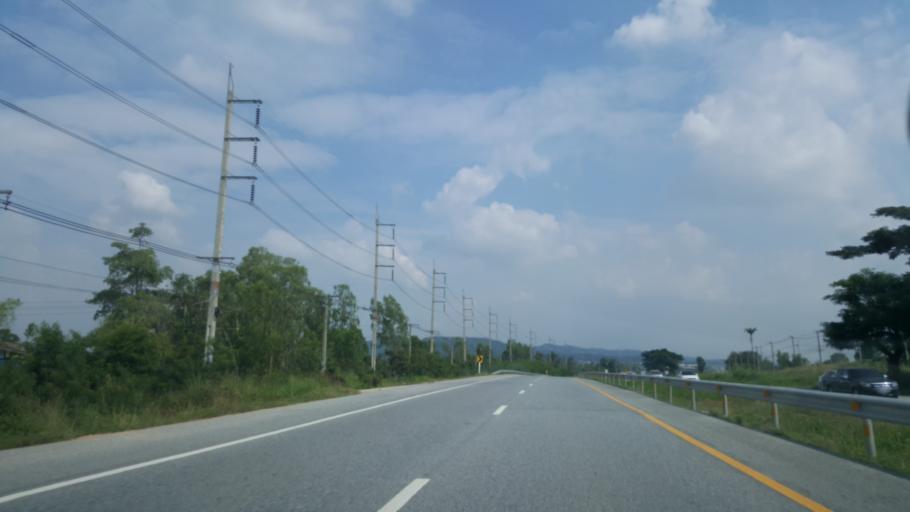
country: TH
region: Chon Buri
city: Ban Talat Bueng
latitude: 12.9314
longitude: 101.0363
